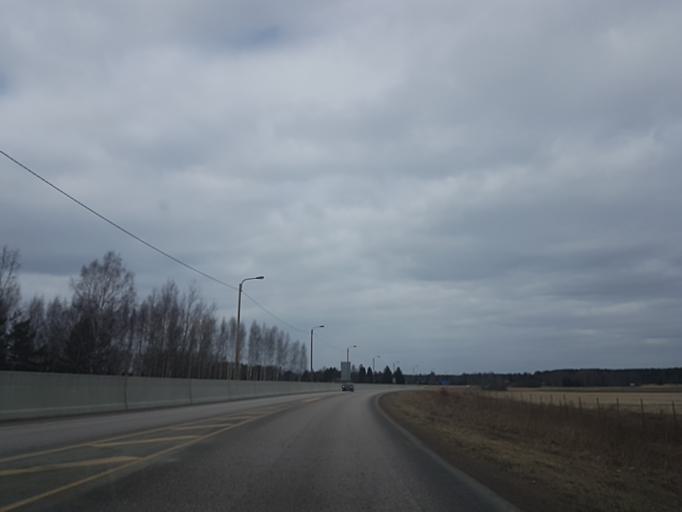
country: FI
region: Kymenlaakso
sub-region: Kotka-Hamina
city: Hamina
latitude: 60.6030
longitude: 27.1865
